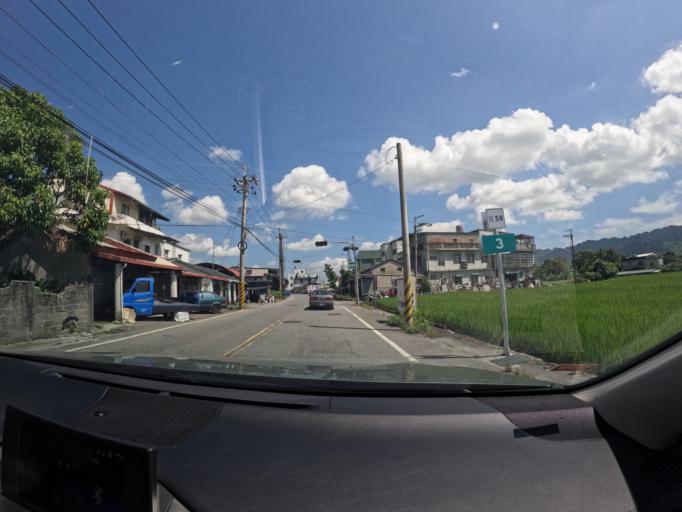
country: TW
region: Taiwan
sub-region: Hualien
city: Hualian
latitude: 23.5784
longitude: 121.3777
